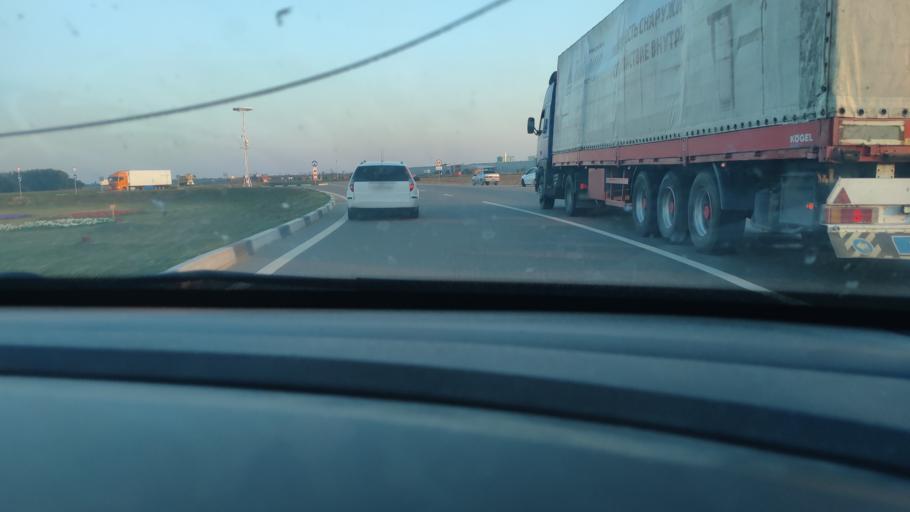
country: RU
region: Krasnodarskiy
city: Timashevsk
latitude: 45.6385
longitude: 38.9707
